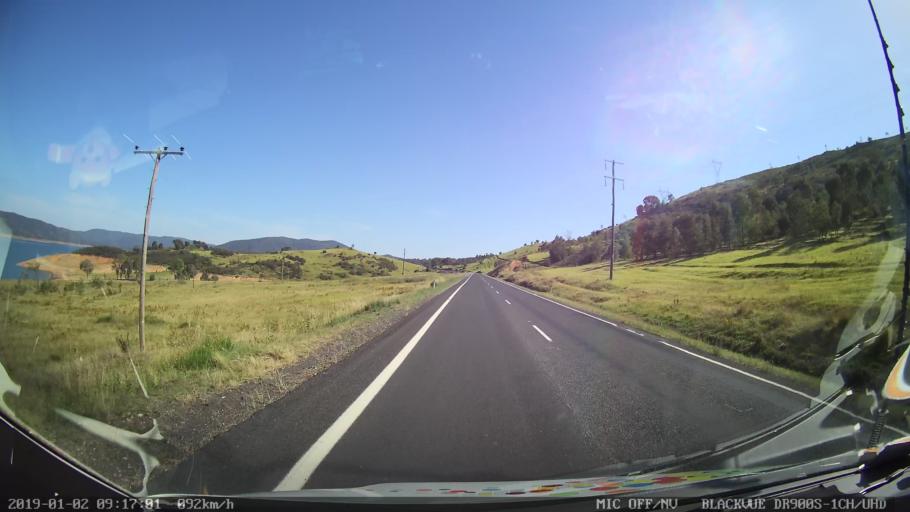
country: AU
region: New South Wales
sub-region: Tumut Shire
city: Tumut
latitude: -35.4466
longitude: 148.2861
